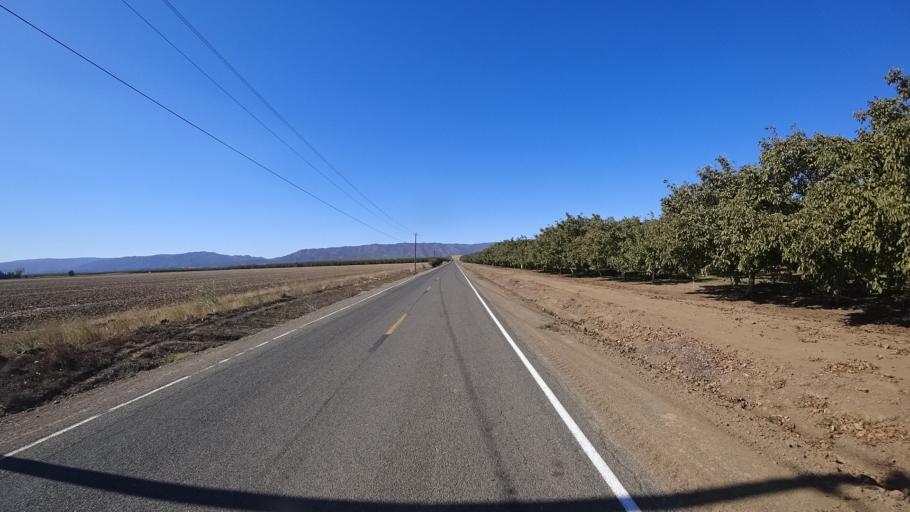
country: US
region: California
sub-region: Yolo County
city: Winters
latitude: 38.5618
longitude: -121.9647
